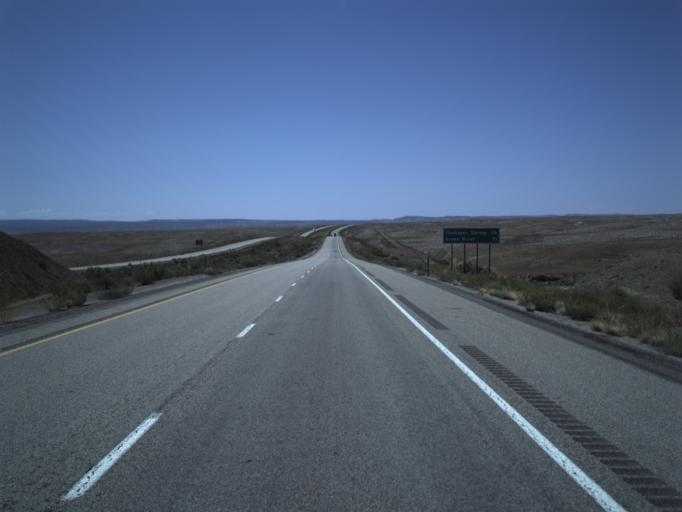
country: US
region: Colorado
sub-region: Mesa County
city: Loma
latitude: 39.0261
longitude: -109.2944
